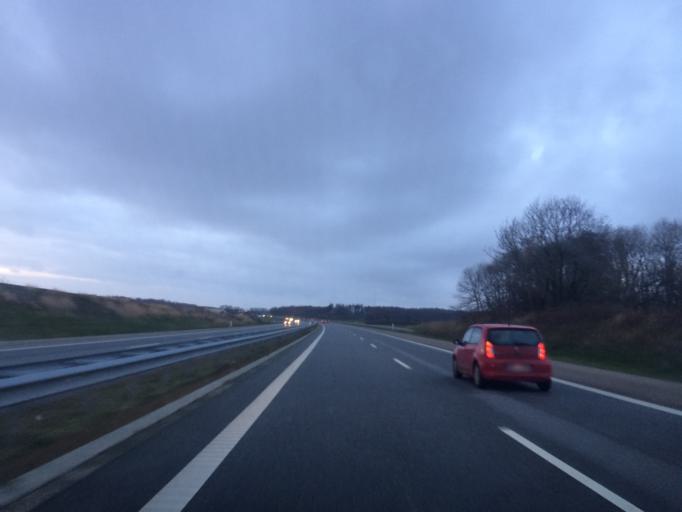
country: DK
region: South Denmark
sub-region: Sonderborg Kommune
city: Grasten
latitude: 54.9587
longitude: 9.6081
